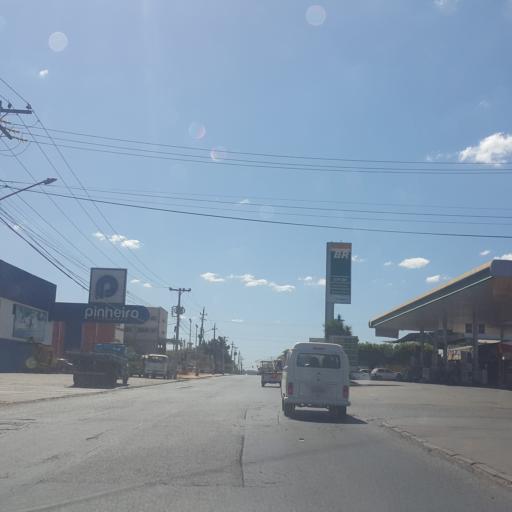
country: BR
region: Federal District
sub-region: Brasilia
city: Brasilia
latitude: -15.8086
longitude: -48.0736
